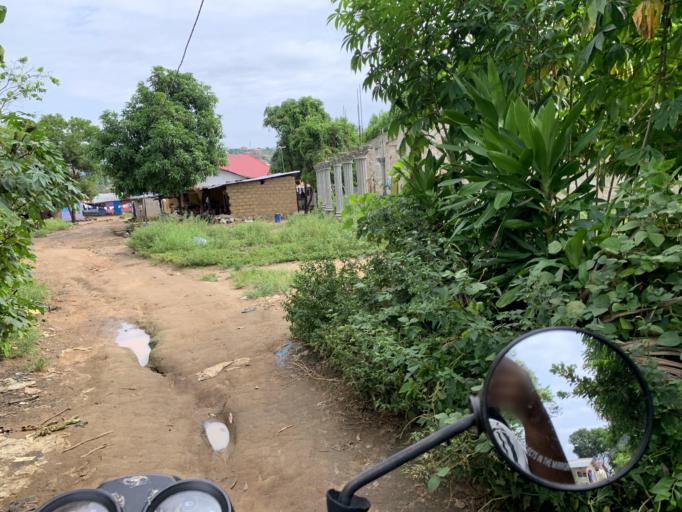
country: SL
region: Western Area
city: Hastings
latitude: 8.3959
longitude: -13.1170
